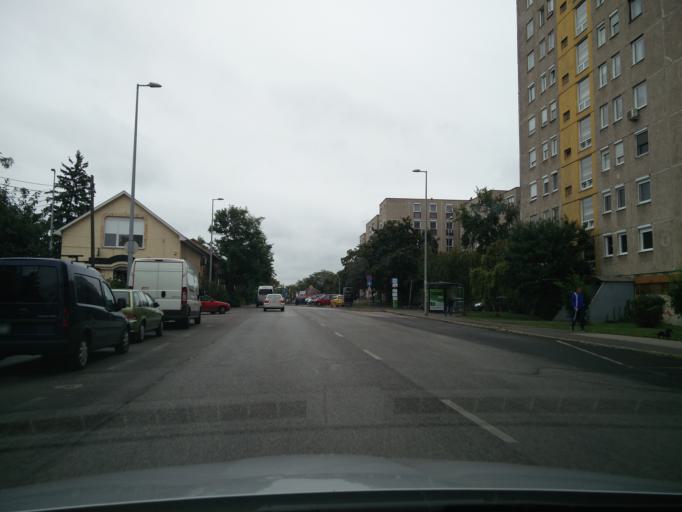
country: HU
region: Budapest
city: Budapest XIX. keruelet
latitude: 47.4589
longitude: 19.1487
